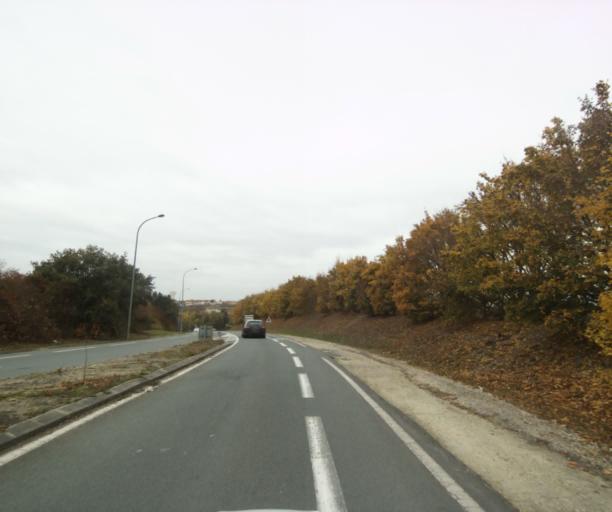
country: FR
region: Poitou-Charentes
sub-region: Departement de la Charente-Maritime
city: Saintes
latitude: 45.7250
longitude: -0.6398
